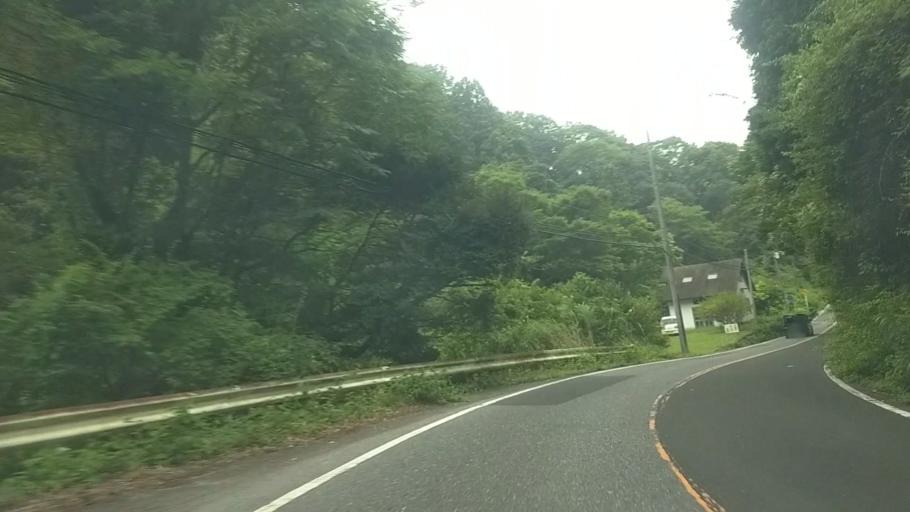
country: JP
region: Chiba
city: Tateyama
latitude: 35.1414
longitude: 139.8963
